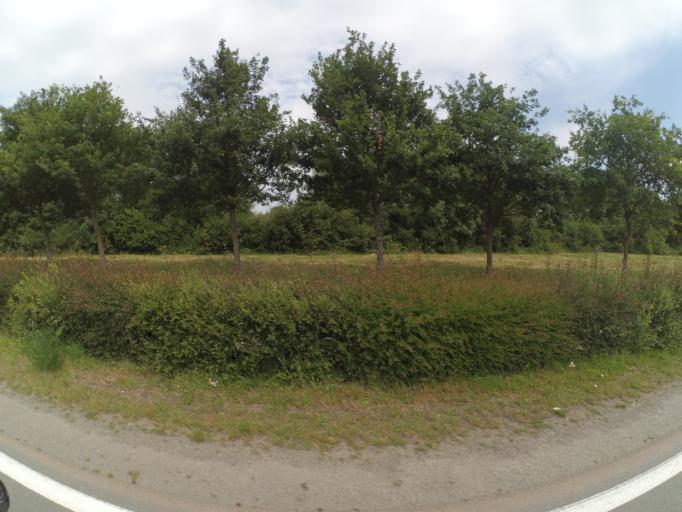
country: FR
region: Pays de la Loire
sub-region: Departement de la Vendee
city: Les Herbiers
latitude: 46.8449
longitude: -1.0083
